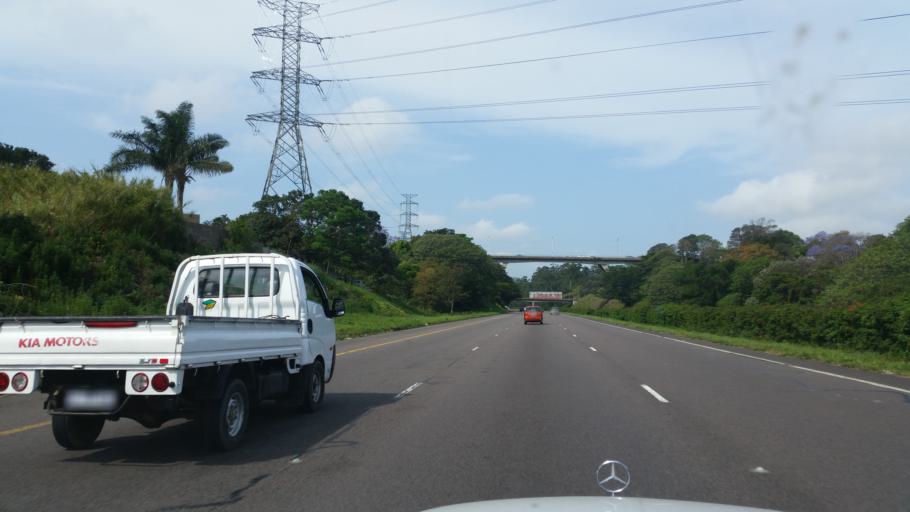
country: ZA
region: KwaZulu-Natal
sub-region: eThekwini Metropolitan Municipality
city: Berea
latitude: -29.8379
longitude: 30.8727
